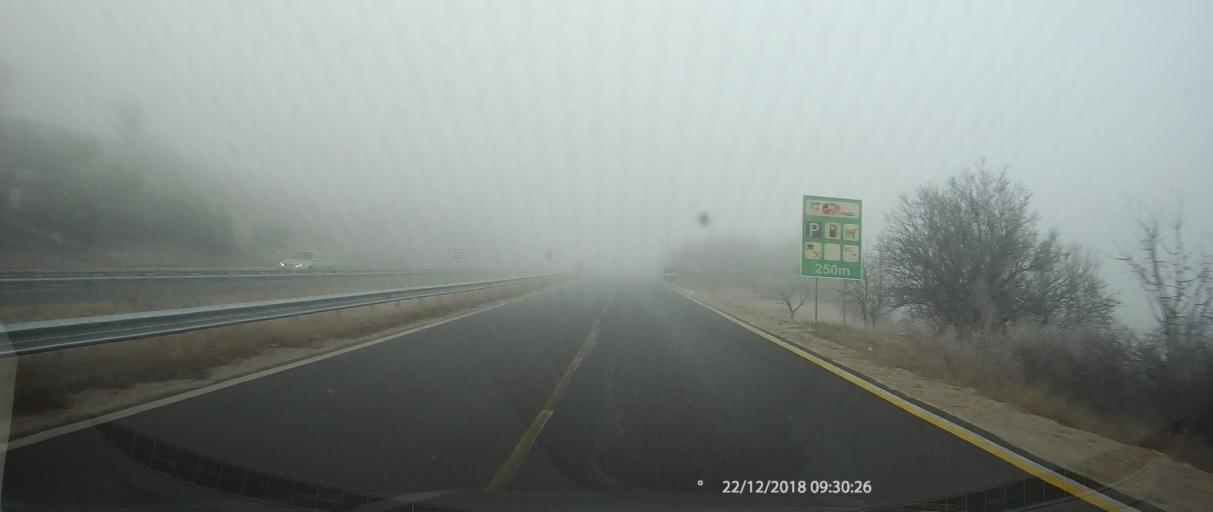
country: MK
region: Kumanovo
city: Romanovce
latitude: 42.1020
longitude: 21.7013
